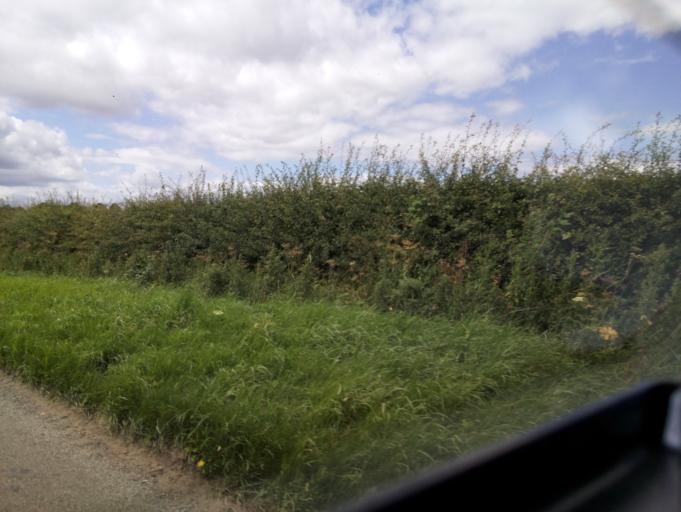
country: GB
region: England
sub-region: Nottinghamshire
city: Cotgrave
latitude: 52.8535
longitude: -1.0480
